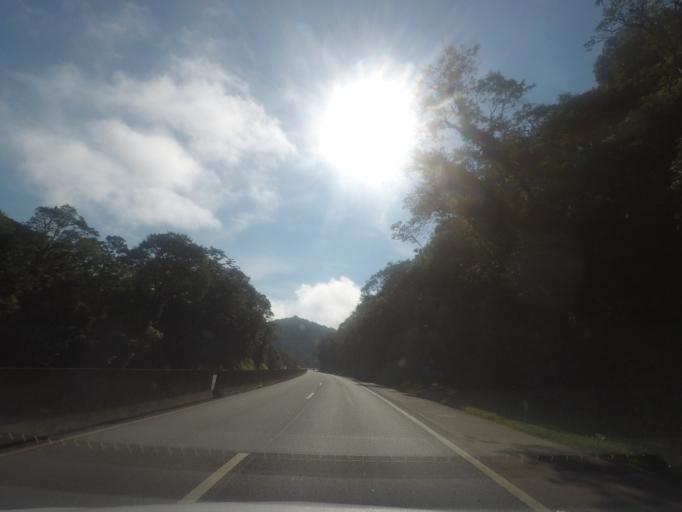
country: BR
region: Parana
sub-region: Piraquara
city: Piraquara
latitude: -25.5950
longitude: -48.8976
